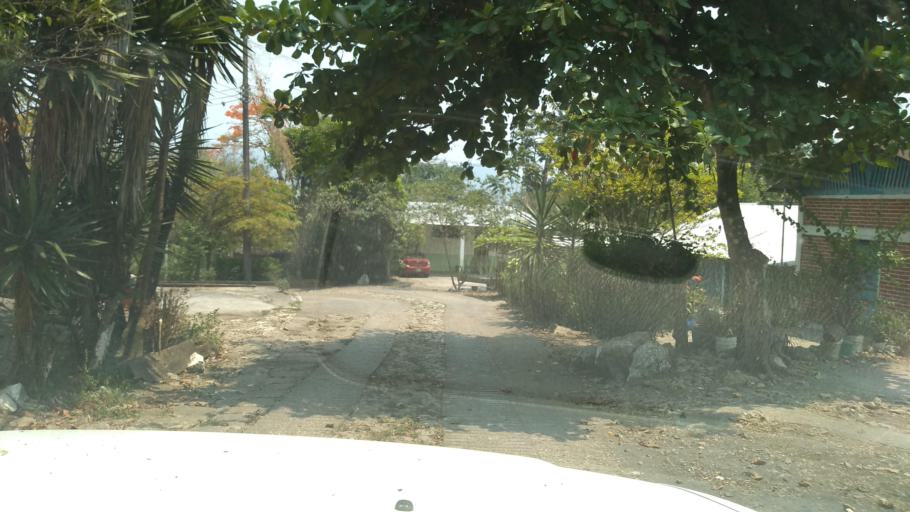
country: MX
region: Veracruz
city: Cosolapa
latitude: 18.5959
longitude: -96.7273
